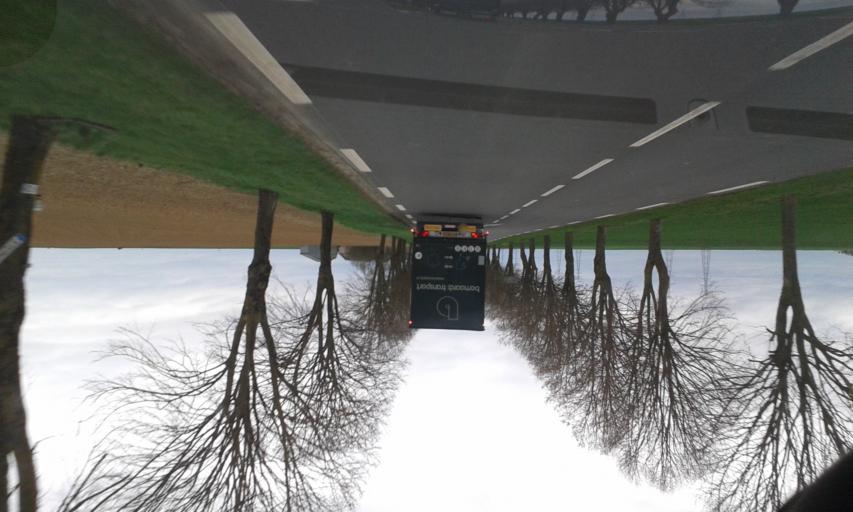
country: FR
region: Centre
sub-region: Departement d'Eure-et-Loir
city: Baigneaux
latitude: 48.1393
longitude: 1.8499
